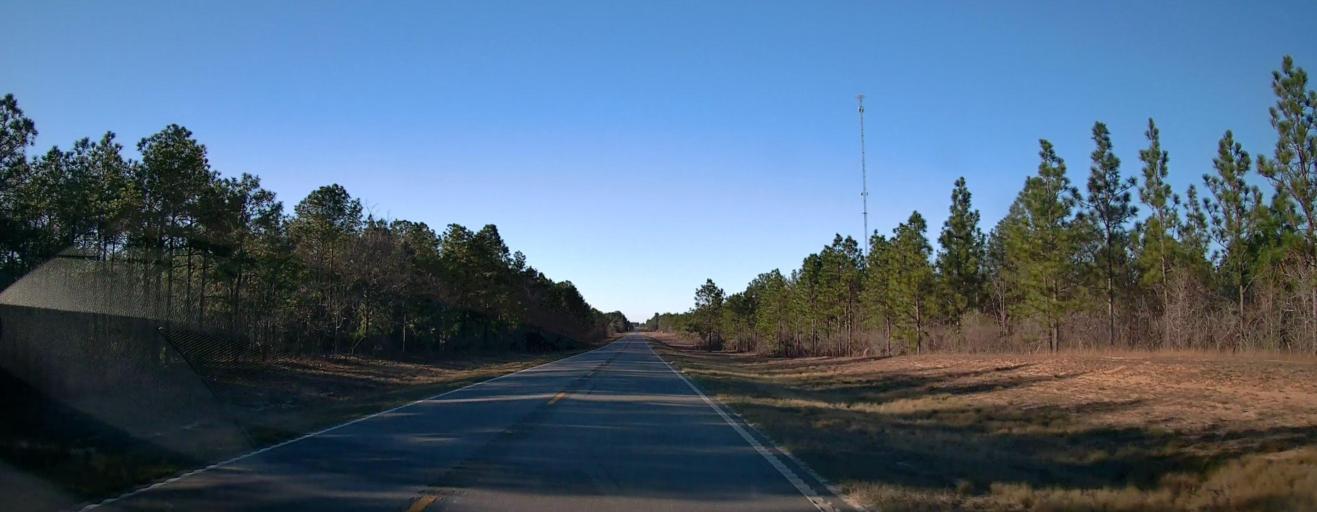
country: US
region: Georgia
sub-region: Talbot County
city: Talbotton
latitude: 32.5680
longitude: -84.4399
